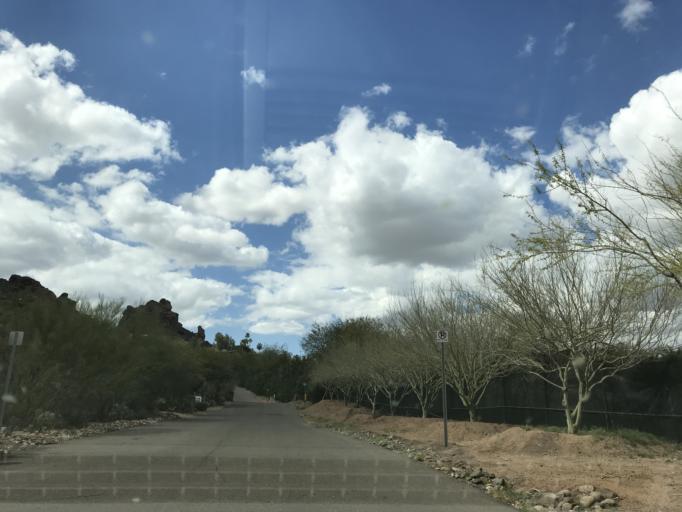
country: US
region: Arizona
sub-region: Maricopa County
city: Paradise Valley
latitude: 33.5213
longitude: -111.9543
